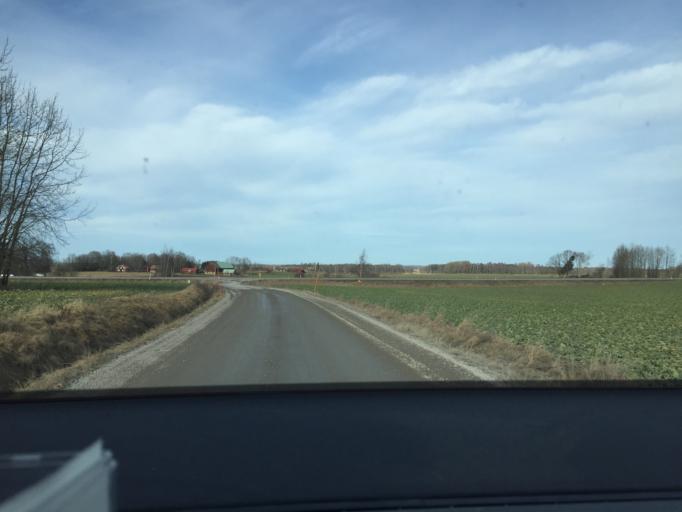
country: SE
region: OErebro
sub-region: Hallsbergs Kommun
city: Skollersta
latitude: 59.1474
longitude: 15.4131
